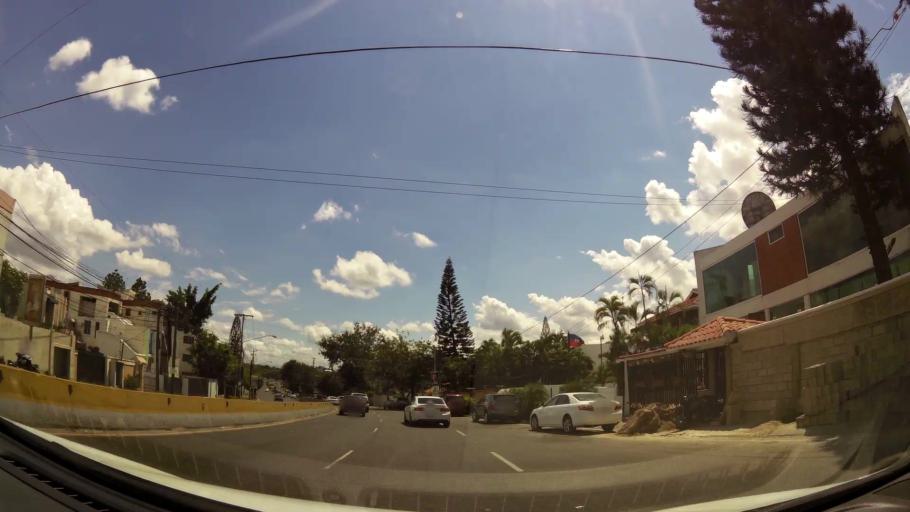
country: DO
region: Santiago
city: Santiago de los Caballeros
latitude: 19.4472
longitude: -70.6884
